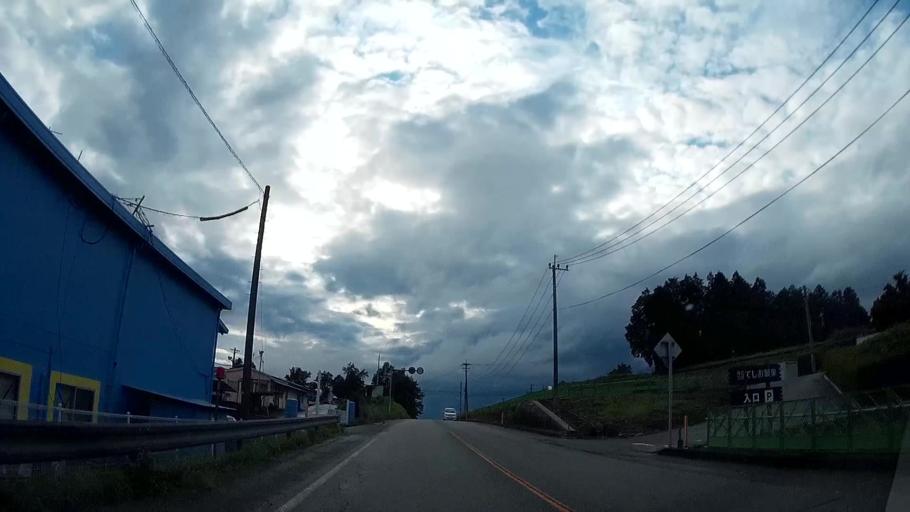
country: JP
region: Kumamoto
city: Ozu
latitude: 32.8780
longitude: 130.9172
